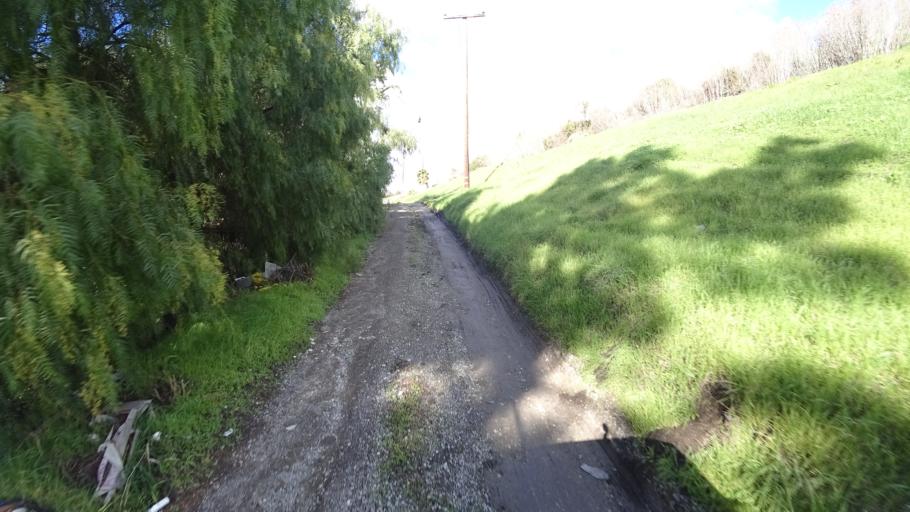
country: US
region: California
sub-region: Alameda County
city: Union City
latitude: 37.6320
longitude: -122.0423
